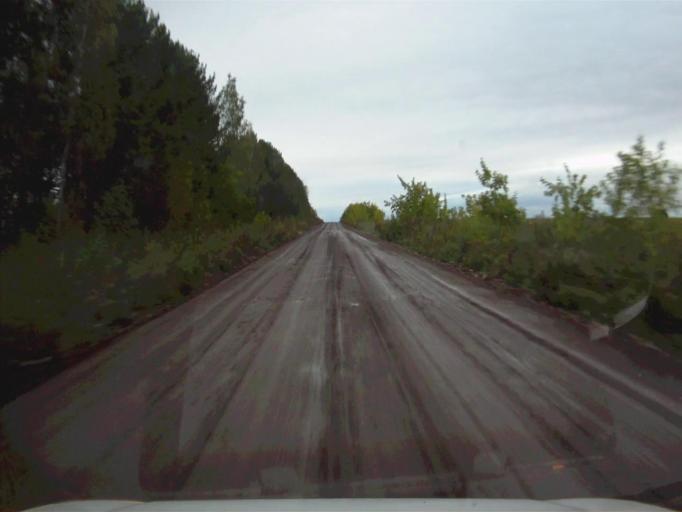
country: RU
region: Sverdlovsk
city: Mikhaylovsk
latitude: 56.1544
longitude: 59.2619
